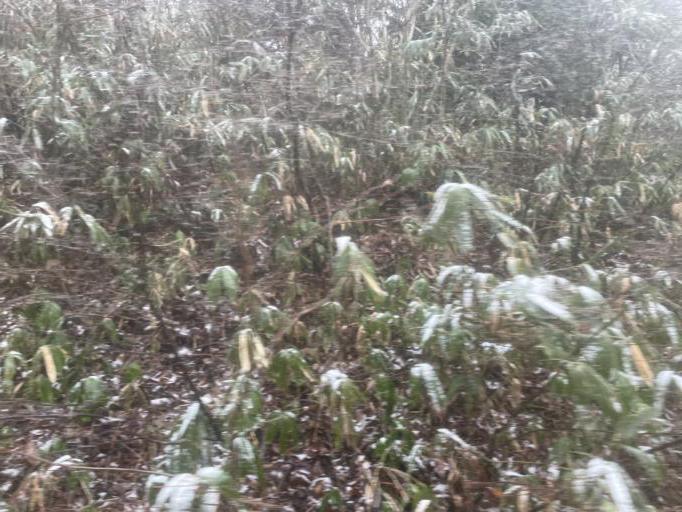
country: JP
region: Aomori
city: Goshogawara
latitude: 41.1013
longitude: 140.5281
